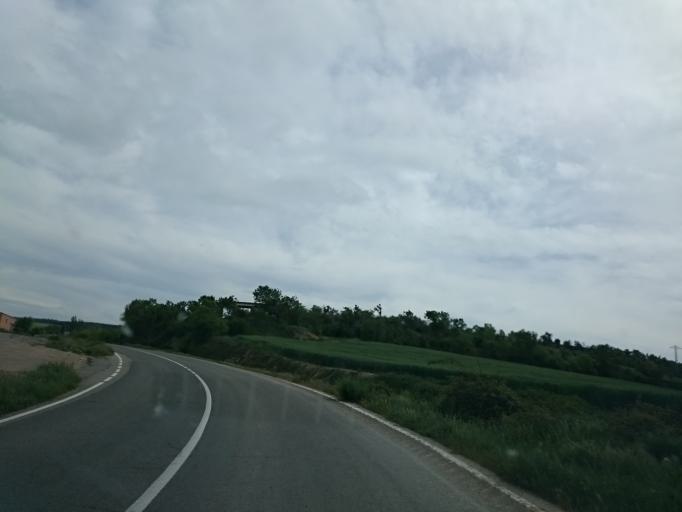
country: ES
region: Catalonia
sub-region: Provincia de Lleida
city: Ivorra
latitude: 41.7735
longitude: 1.3874
